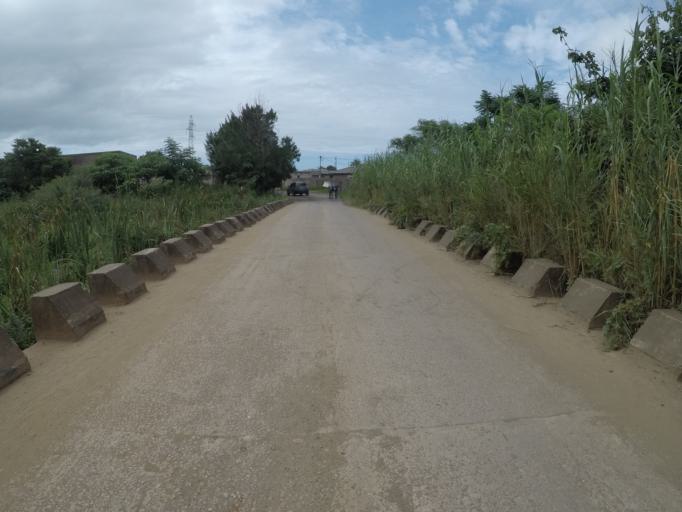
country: ZA
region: KwaZulu-Natal
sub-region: uThungulu District Municipality
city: eSikhawini
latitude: -28.8591
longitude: 31.9169
